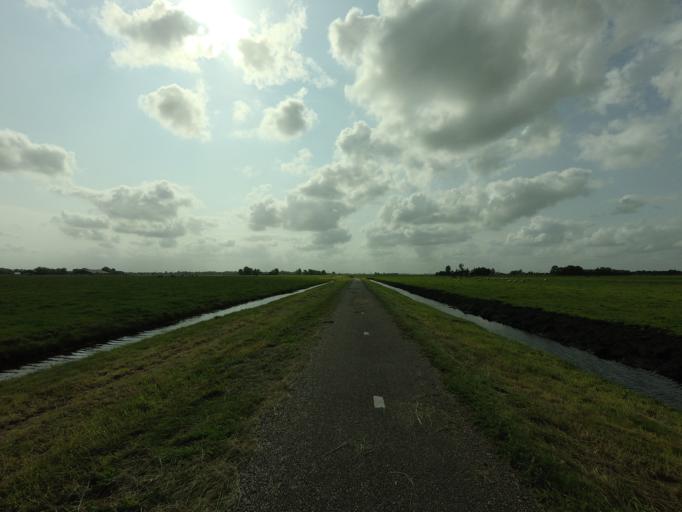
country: NL
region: North Holland
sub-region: Gemeente Waterland
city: Broek in Waterland
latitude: 52.4501
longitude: 5.0091
